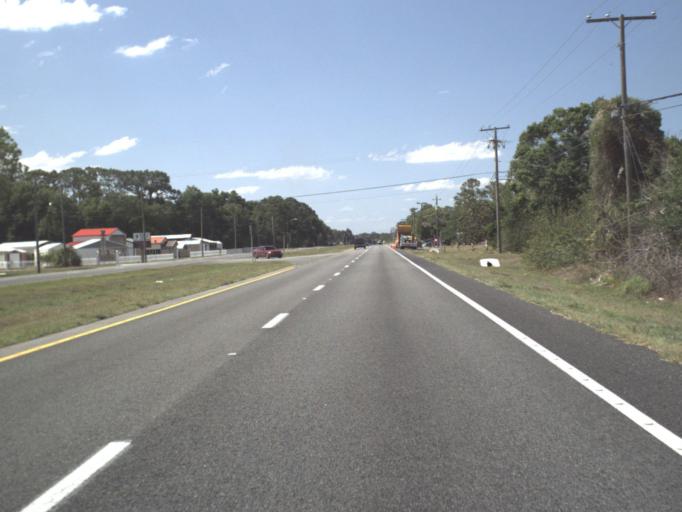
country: US
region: Florida
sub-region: Brevard County
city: Mims
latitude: 28.6802
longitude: -80.8517
